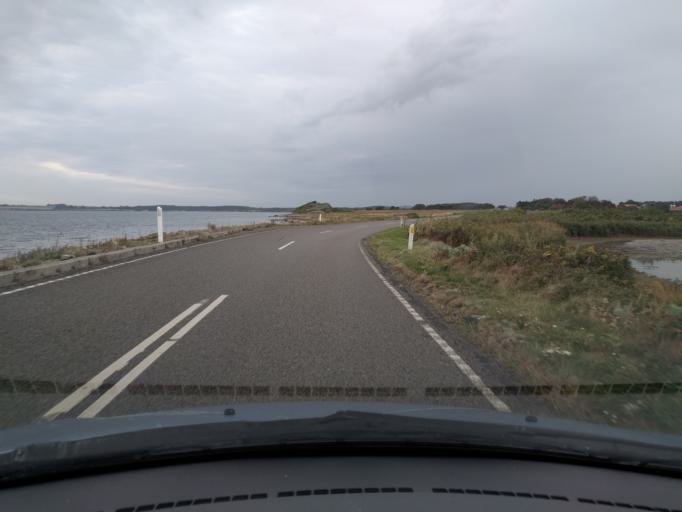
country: DK
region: South Denmark
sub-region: Assens Kommune
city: Assens
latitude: 55.1875
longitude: 9.9841
